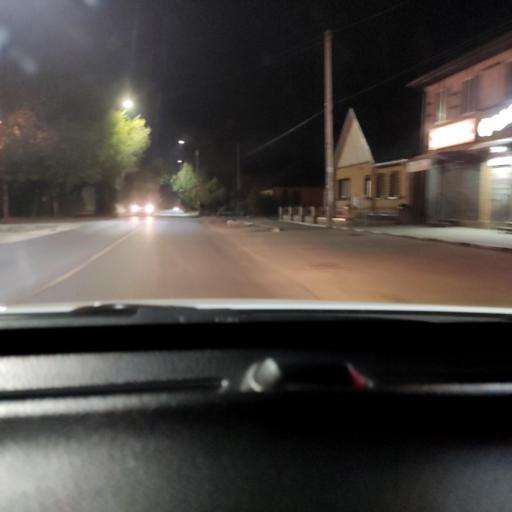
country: RU
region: Voronezj
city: Somovo
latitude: 51.7356
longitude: 39.2669
